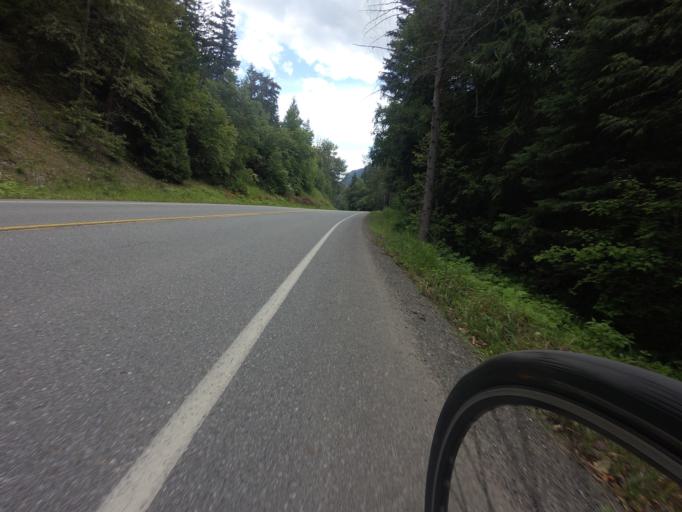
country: CA
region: British Columbia
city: Lillooet
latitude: 50.6187
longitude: -122.1035
